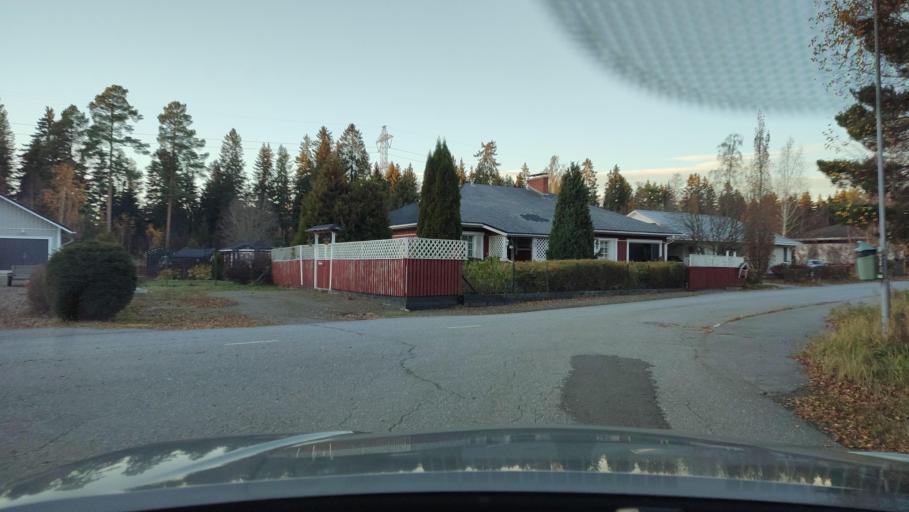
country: FI
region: Ostrobothnia
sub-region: Sydosterbotten
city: Kristinestad
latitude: 62.2804
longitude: 21.3535
